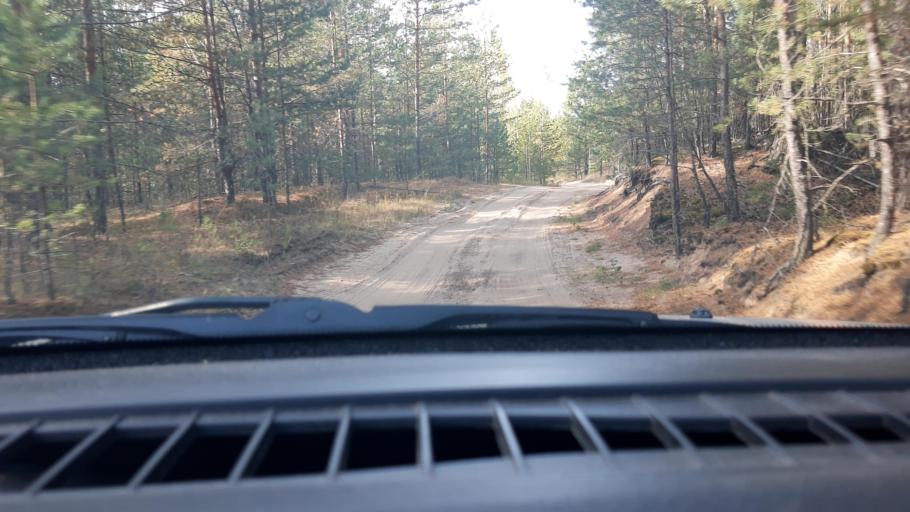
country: RU
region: Nizjnij Novgorod
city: Lukino
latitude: 56.3931
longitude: 43.6252
